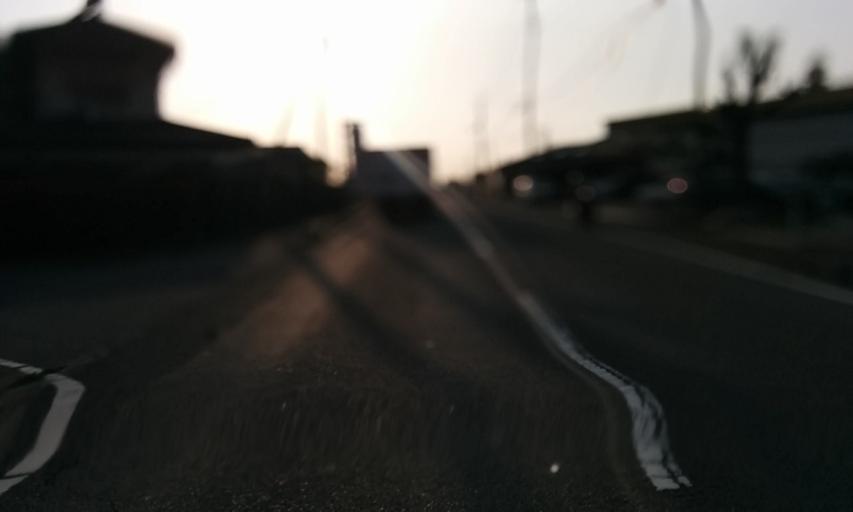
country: JP
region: Ehime
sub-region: Shikoku-chuo Shi
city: Matsuyama
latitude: 33.7780
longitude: 132.8344
